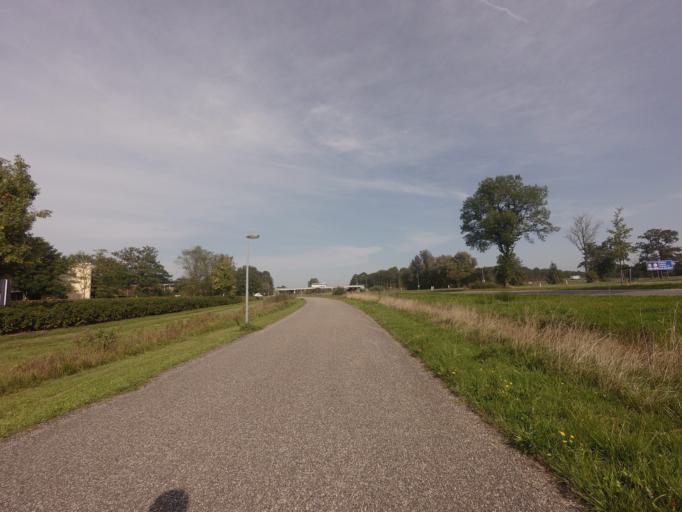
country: NL
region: Groningen
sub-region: Gemeente Leek
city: Leek
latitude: 53.1828
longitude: 6.3800
